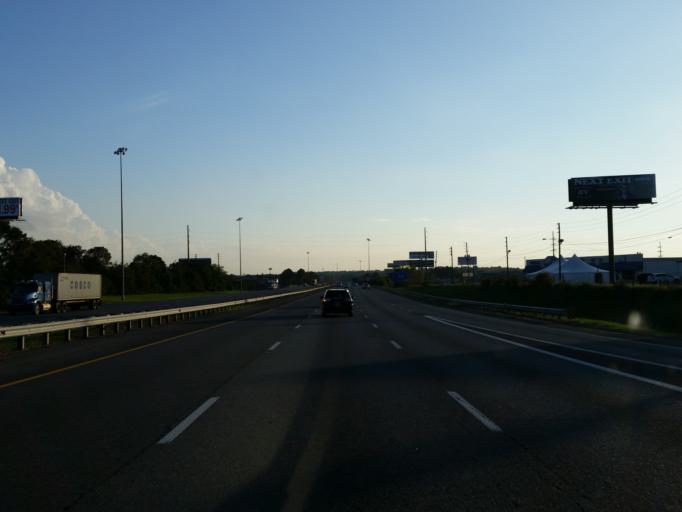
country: US
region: Georgia
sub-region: Houston County
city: Perry
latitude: 32.4687
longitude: -83.7452
